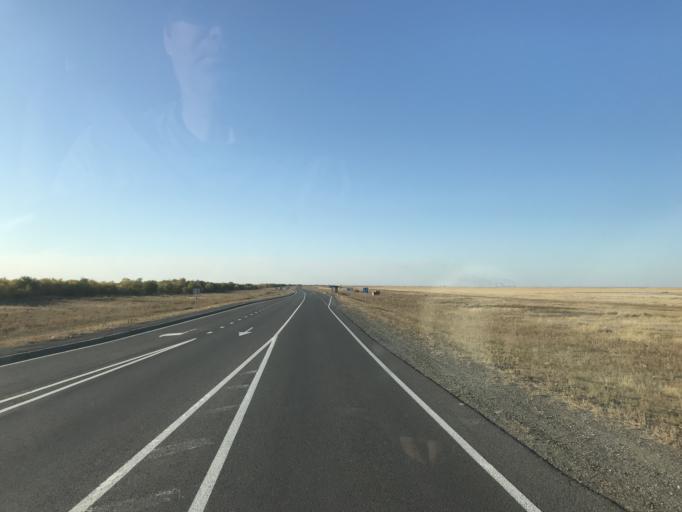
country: KZ
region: Pavlodar
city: Aksu
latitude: 52.0181
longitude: 77.2330
